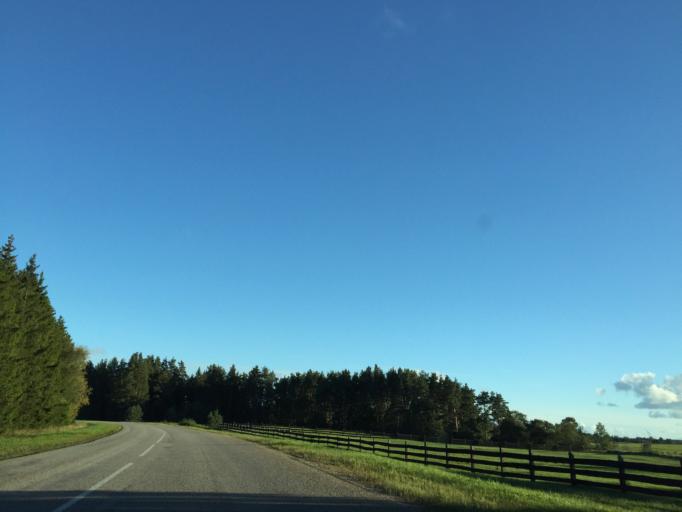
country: LV
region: Kuldigas Rajons
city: Kuldiga
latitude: 56.9148
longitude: 22.0554
